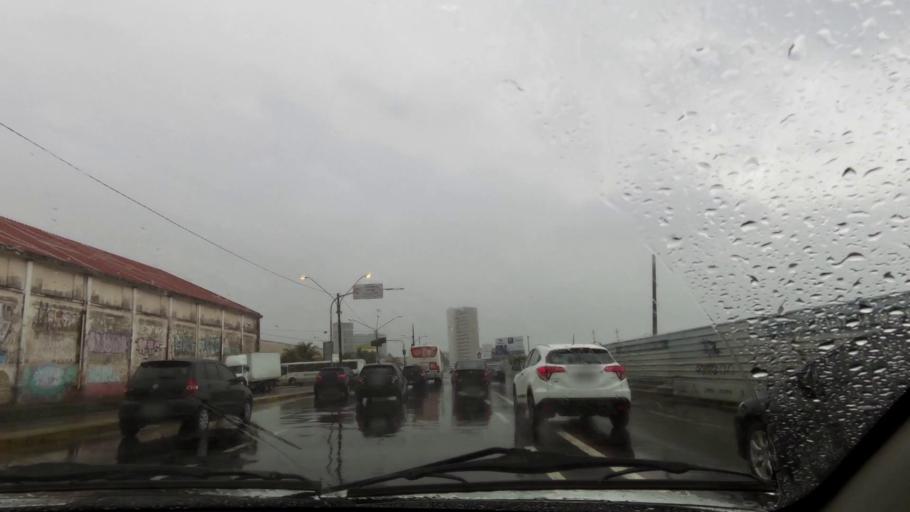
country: BR
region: Pernambuco
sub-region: Recife
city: Recife
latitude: -8.0701
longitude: -34.8755
